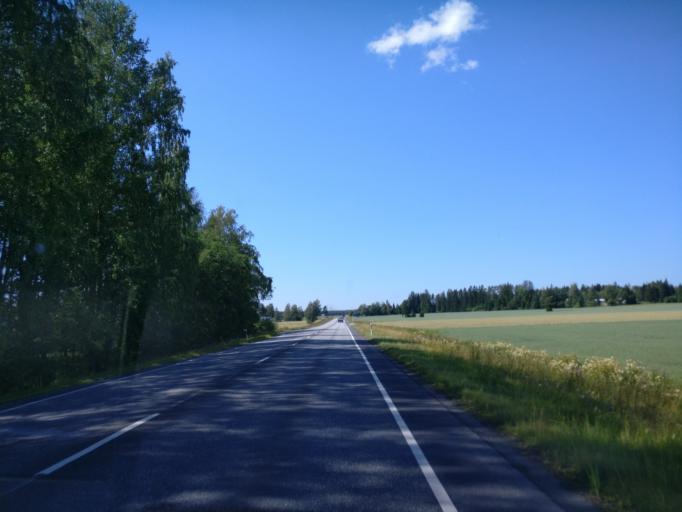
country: FI
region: Satakunta
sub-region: Pori
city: Nakkila
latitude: 61.4589
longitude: 22.0225
